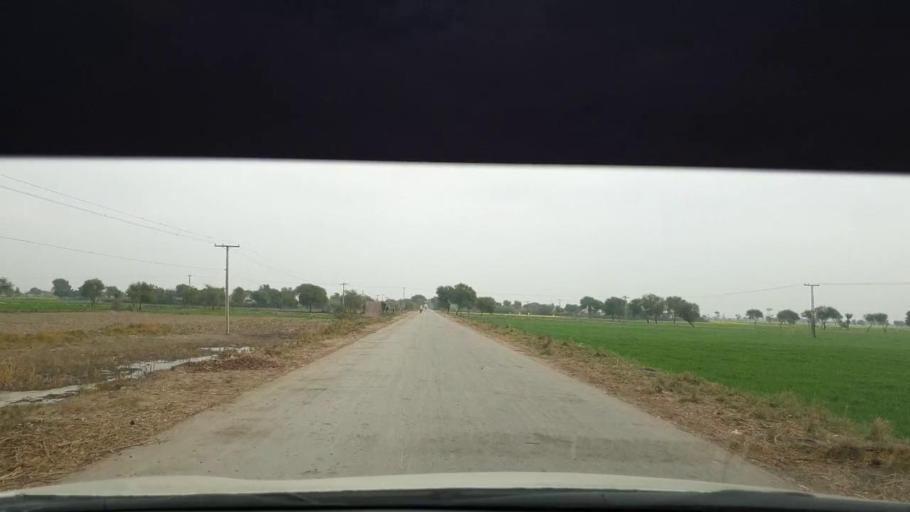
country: PK
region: Sindh
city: Berani
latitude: 25.7771
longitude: 68.8943
